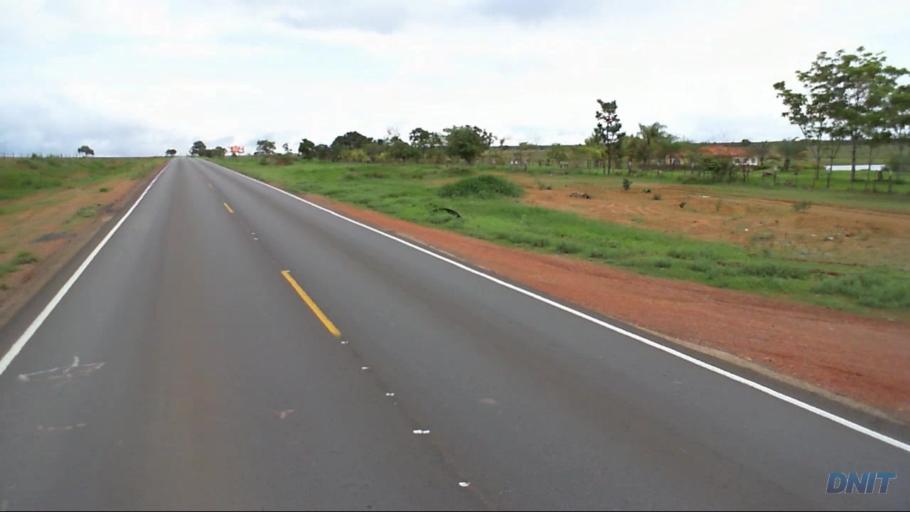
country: BR
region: Goias
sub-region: Padre Bernardo
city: Padre Bernardo
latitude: -15.2854
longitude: -48.2522
